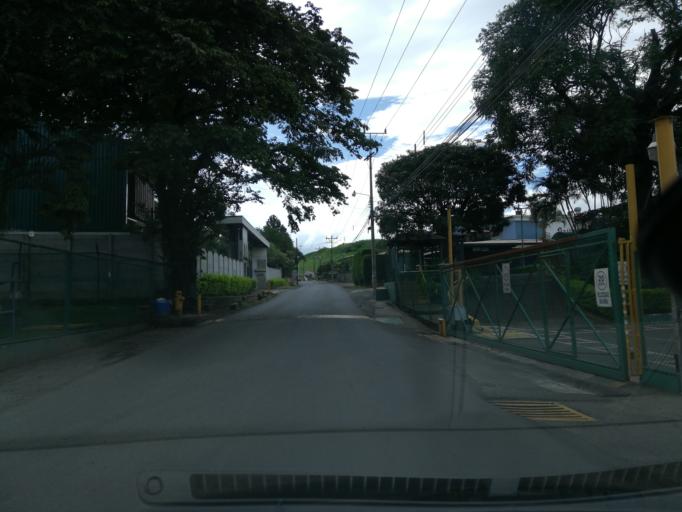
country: CR
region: Alajuela
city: Alajuela
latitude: 9.9959
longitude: -84.2188
